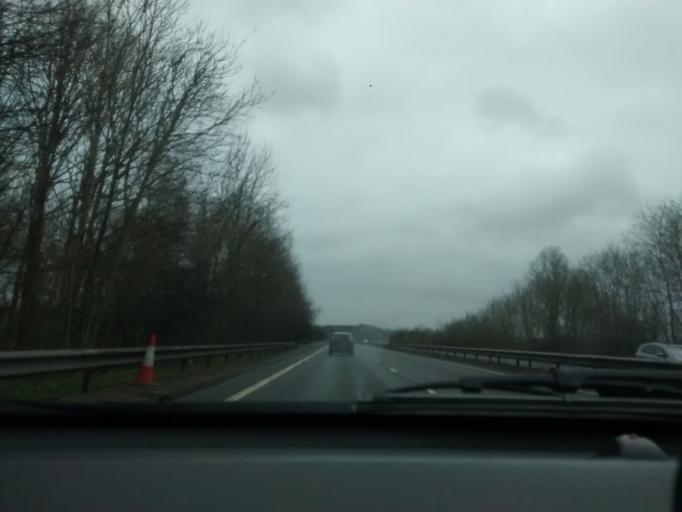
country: GB
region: England
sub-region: Suffolk
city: Needham Market
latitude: 52.1689
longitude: 1.0548
